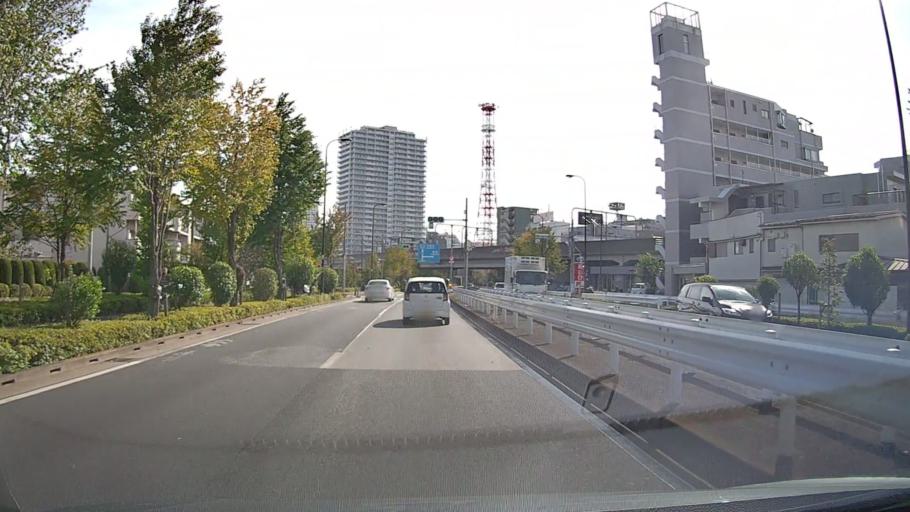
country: JP
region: Saitama
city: Wako
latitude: 35.7383
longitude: 139.6435
